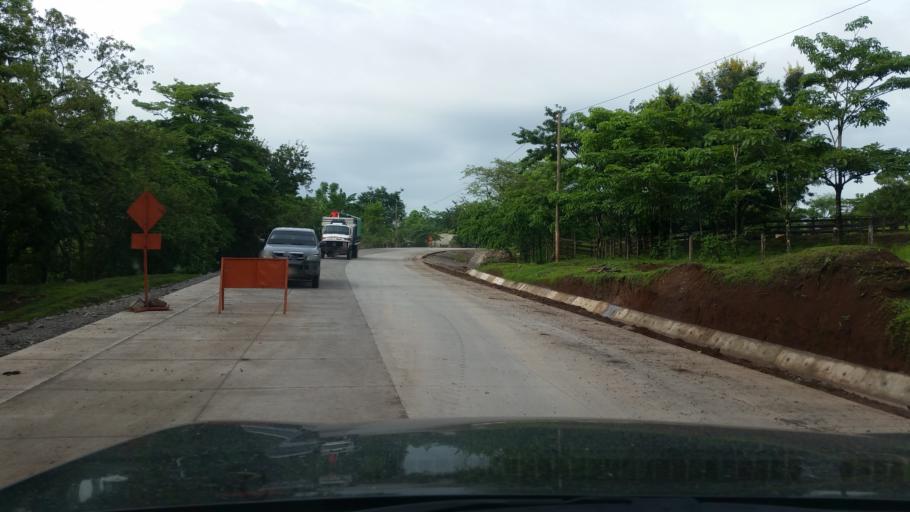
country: NI
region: Matagalpa
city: Rio Blanco
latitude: 13.1186
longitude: -85.0600
